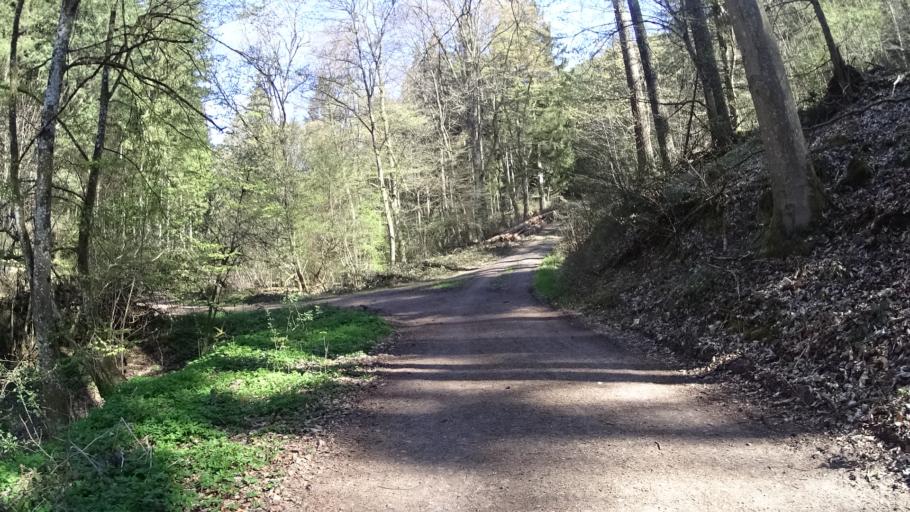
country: DE
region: Rheinland-Pfalz
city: Lambrecht
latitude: 49.3835
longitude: 8.0708
